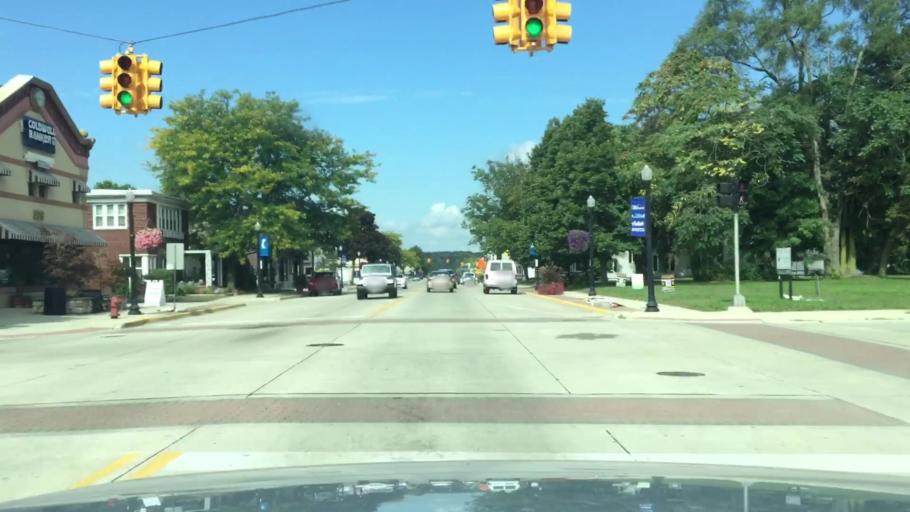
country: US
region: Michigan
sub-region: Wayne County
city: Belleville
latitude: 42.2072
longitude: -83.4889
